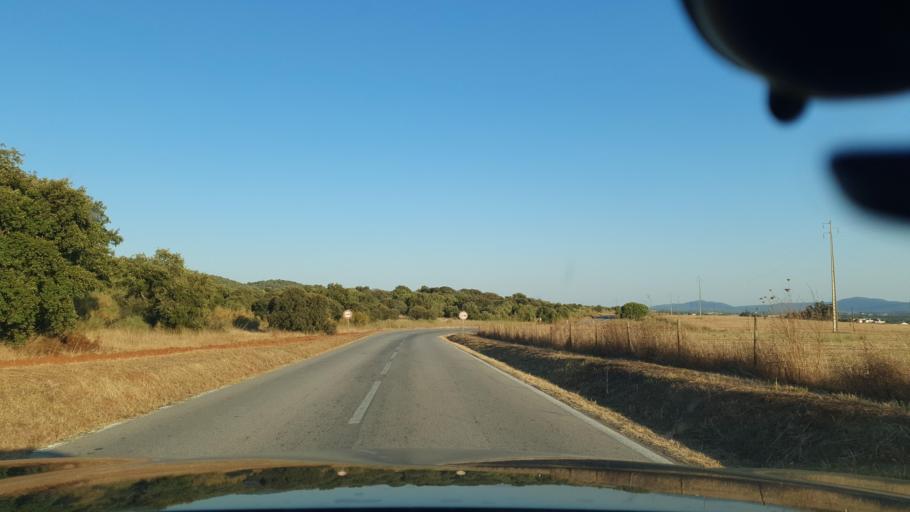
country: PT
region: Evora
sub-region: Estremoz
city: Estremoz
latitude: 38.8850
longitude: -7.6472
